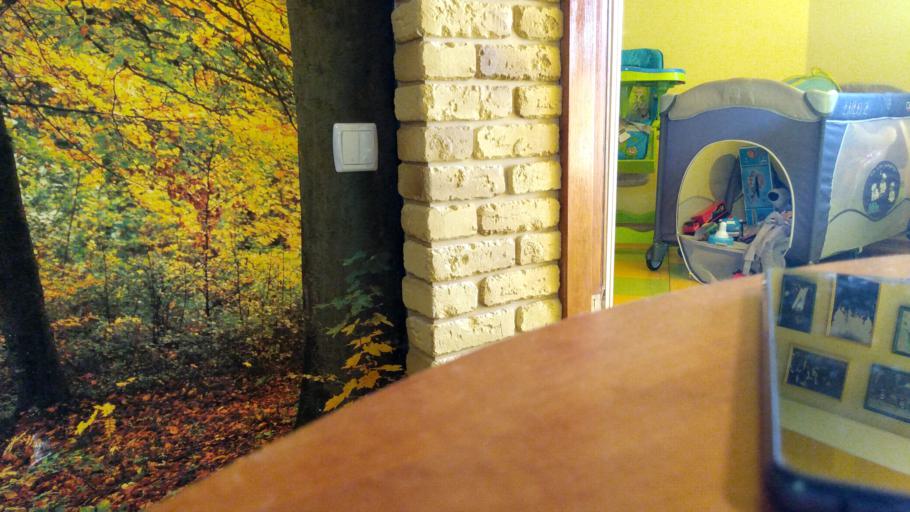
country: RU
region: Tverskaya
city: Kalashnikovo
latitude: 57.3539
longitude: 35.2409
